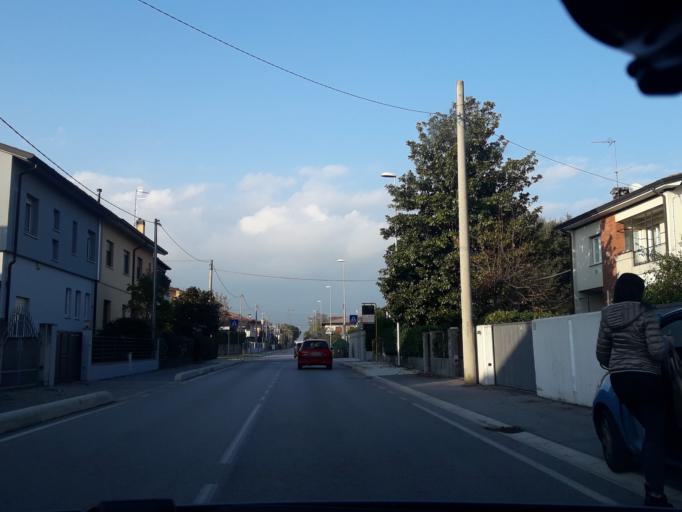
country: IT
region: Friuli Venezia Giulia
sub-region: Provincia di Udine
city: Feletto Umberto
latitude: 46.0899
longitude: 13.2430
